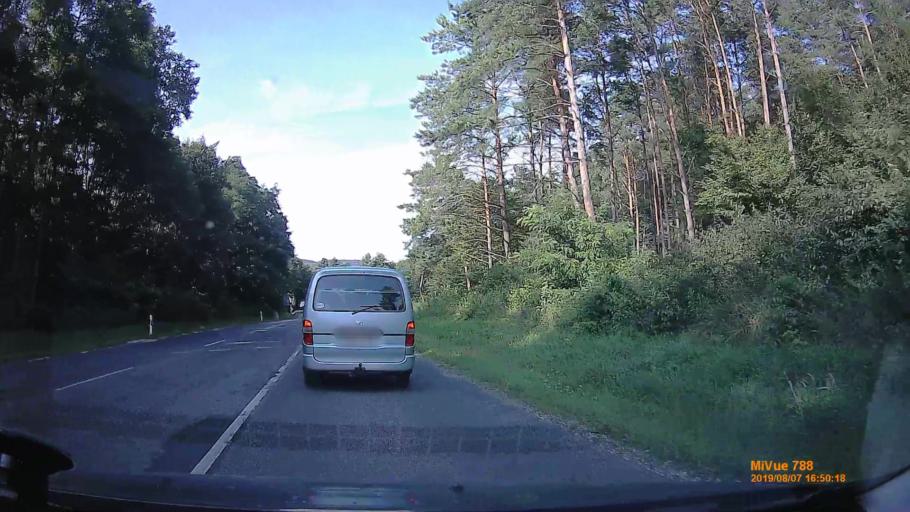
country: HU
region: Zala
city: Lenti
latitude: 46.6819
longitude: 16.6713
